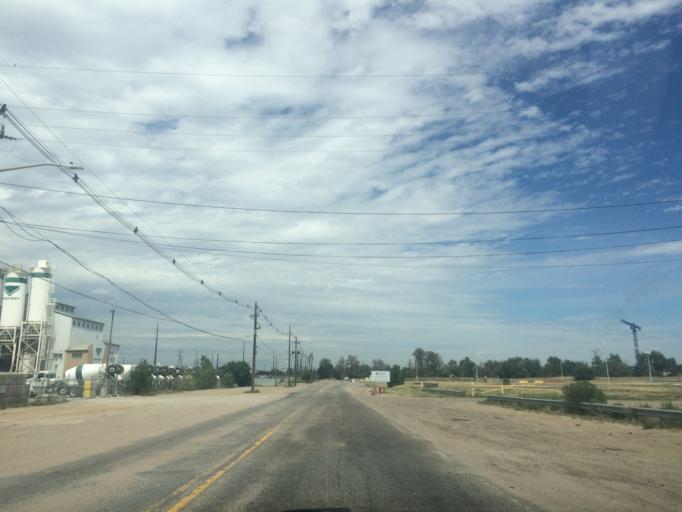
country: US
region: Colorado
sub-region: Adams County
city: Commerce City
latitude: 39.8032
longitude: -104.9593
